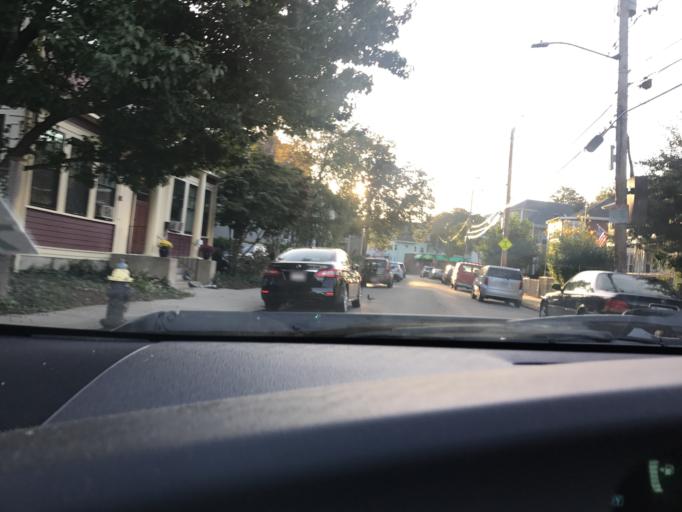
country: US
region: Massachusetts
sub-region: Norfolk County
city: Brookline
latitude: 42.3580
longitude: -71.1343
